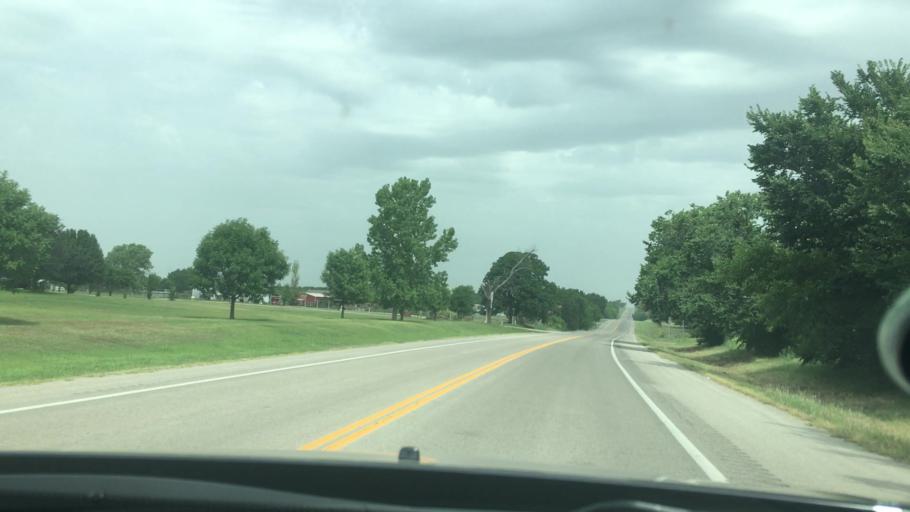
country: US
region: Oklahoma
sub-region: Garvin County
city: Pauls Valley
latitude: 34.8443
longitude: -97.2764
